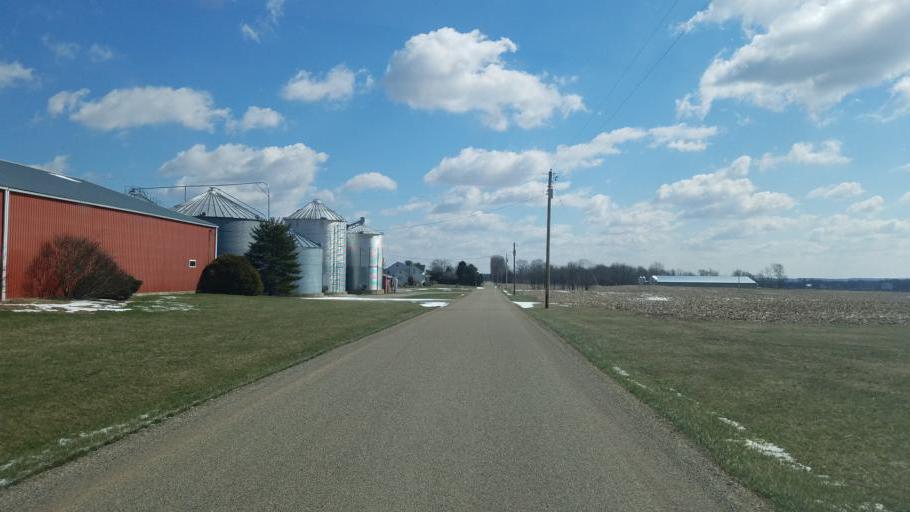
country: US
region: Ohio
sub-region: Licking County
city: Utica
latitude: 40.2898
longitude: -82.5295
